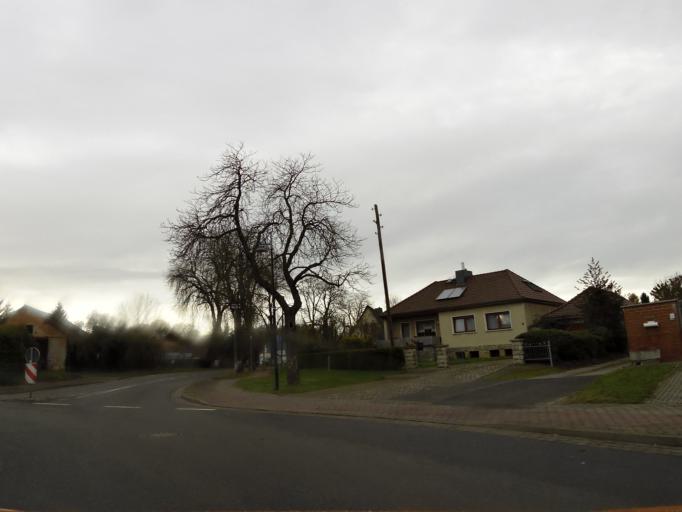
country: DE
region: Saxony-Anhalt
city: Gardelegen
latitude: 52.5260
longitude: 11.3824
